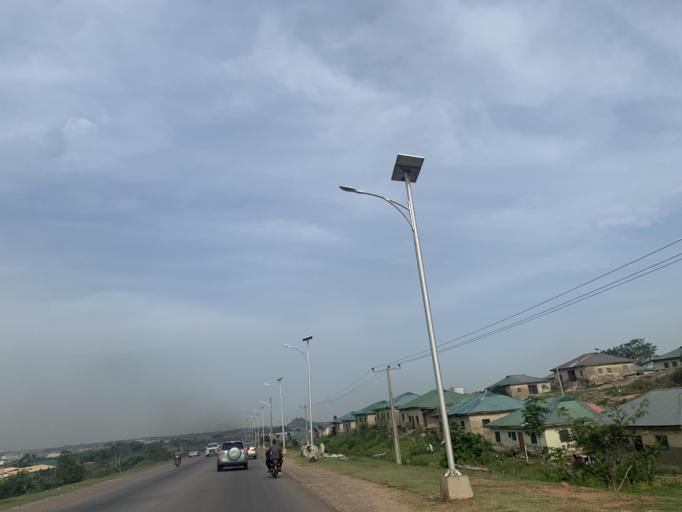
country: NG
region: Abuja Federal Capital Territory
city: Abuja
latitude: 9.0401
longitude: 7.3987
